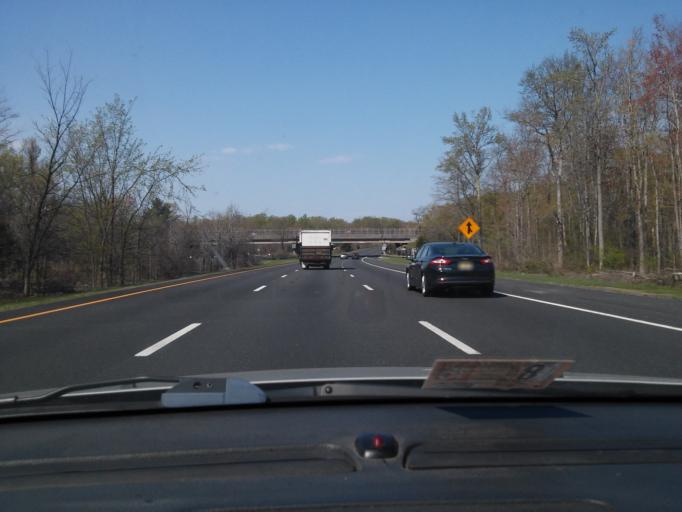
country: US
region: New Jersey
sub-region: Somerset County
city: Watchung
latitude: 40.6525
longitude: -74.4517
